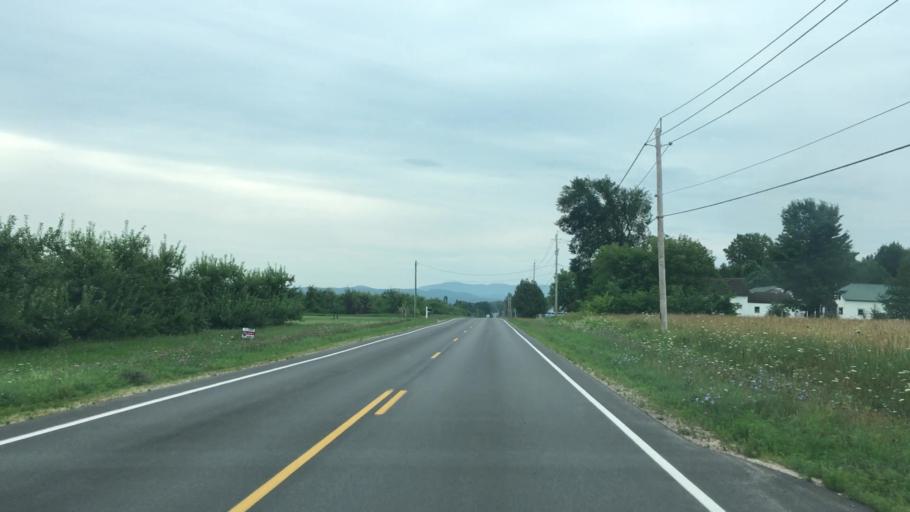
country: US
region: New York
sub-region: Clinton County
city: Peru
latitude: 44.6020
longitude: -73.5744
